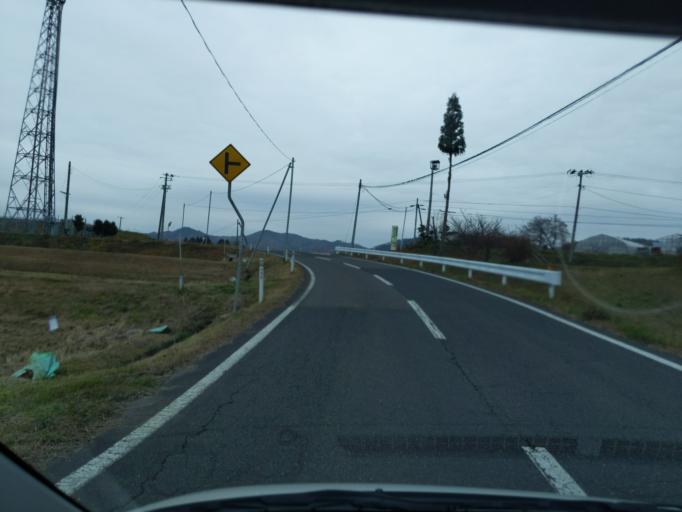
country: JP
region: Iwate
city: Kitakami
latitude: 39.2540
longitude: 141.2078
